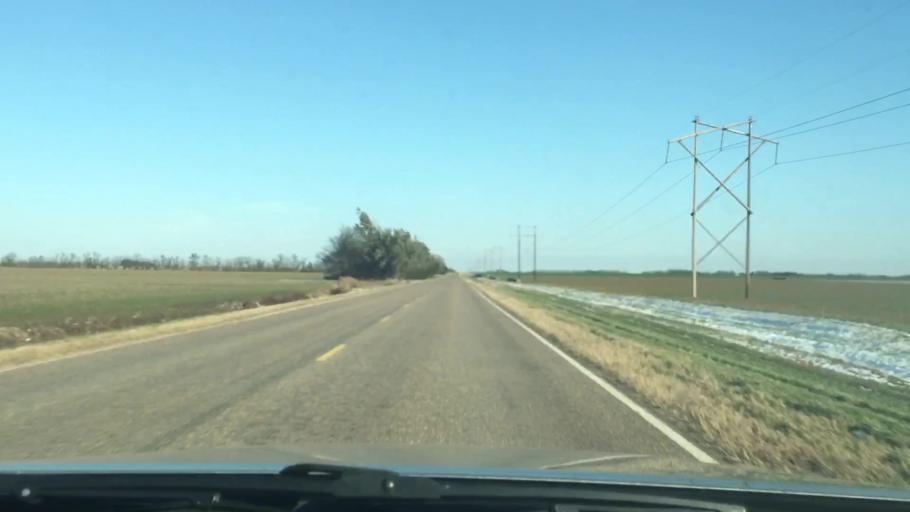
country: US
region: Kansas
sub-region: Rice County
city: Lyons
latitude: 38.2895
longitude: -98.1170
